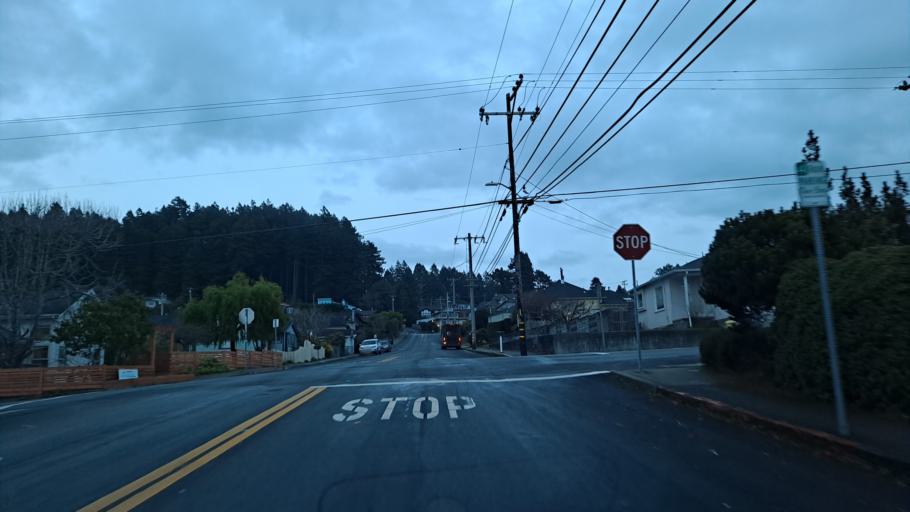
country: US
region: California
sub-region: Humboldt County
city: Arcata
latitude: 40.8688
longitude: -124.0782
